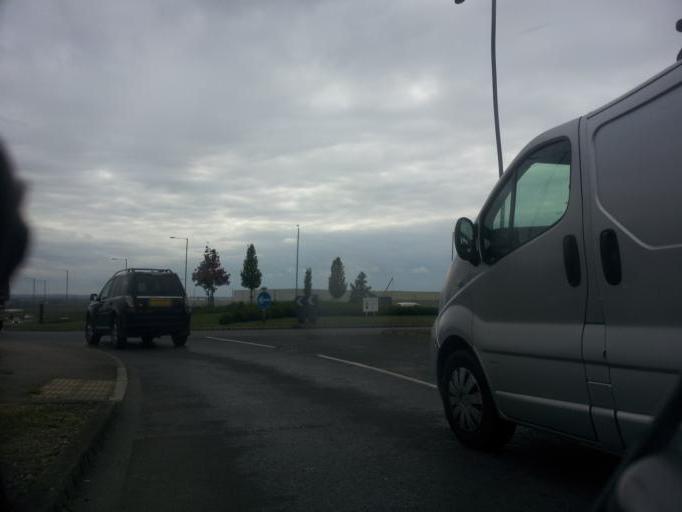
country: GB
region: England
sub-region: Kent
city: Queenborough
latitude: 51.4094
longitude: 0.7716
